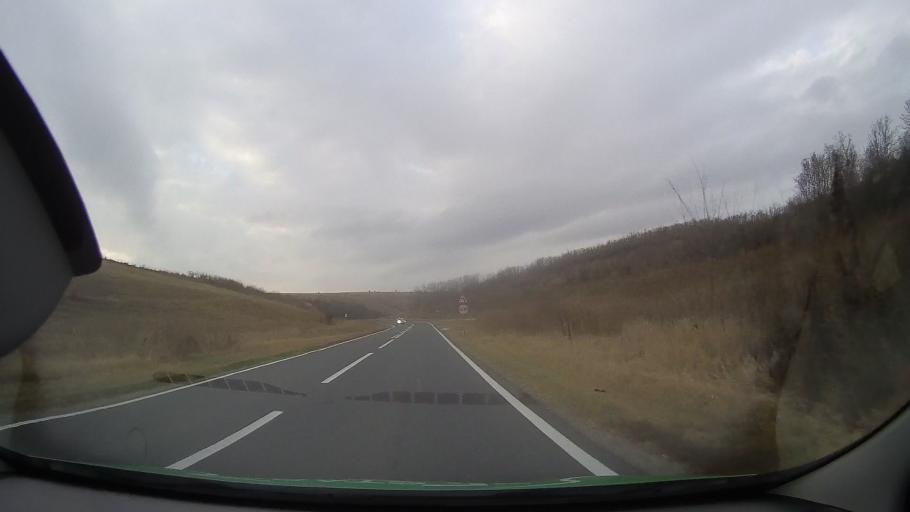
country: RO
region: Constanta
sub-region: Comuna Deleni
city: Deleni
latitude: 44.1016
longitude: 28.0275
